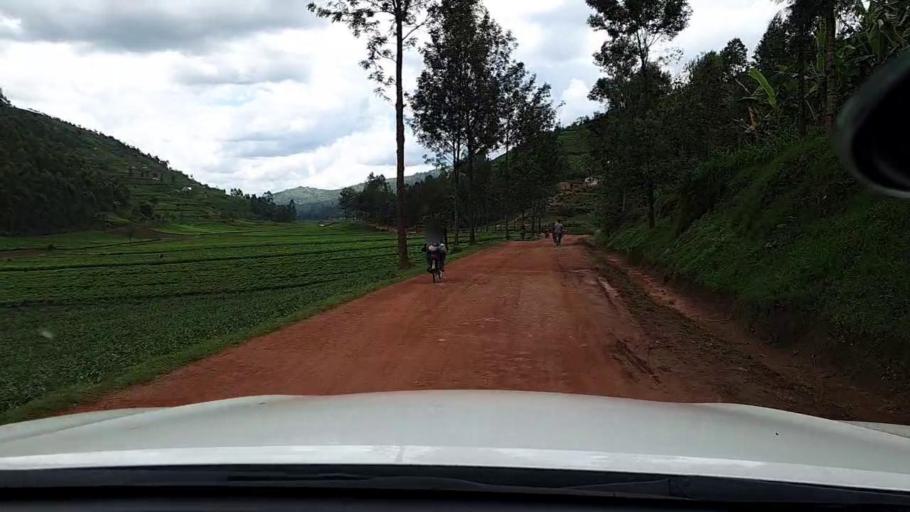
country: RW
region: Northern Province
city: Byumba
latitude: -1.6583
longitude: 29.9120
